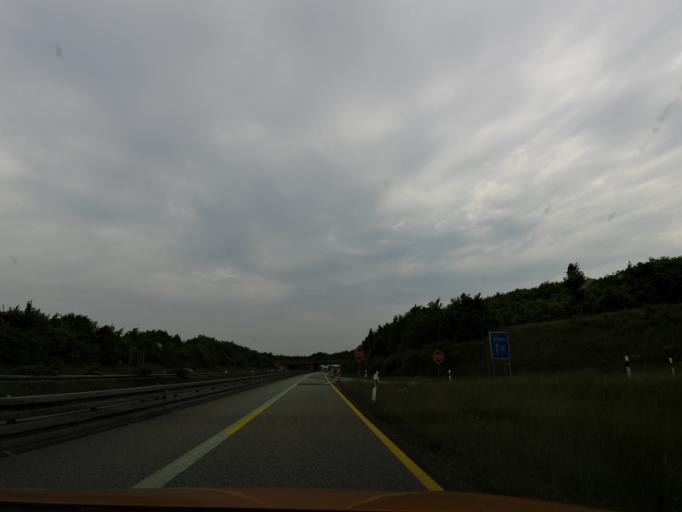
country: DE
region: Mecklenburg-Vorpommern
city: Bobitz
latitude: 53.8542
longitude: 11.3805
